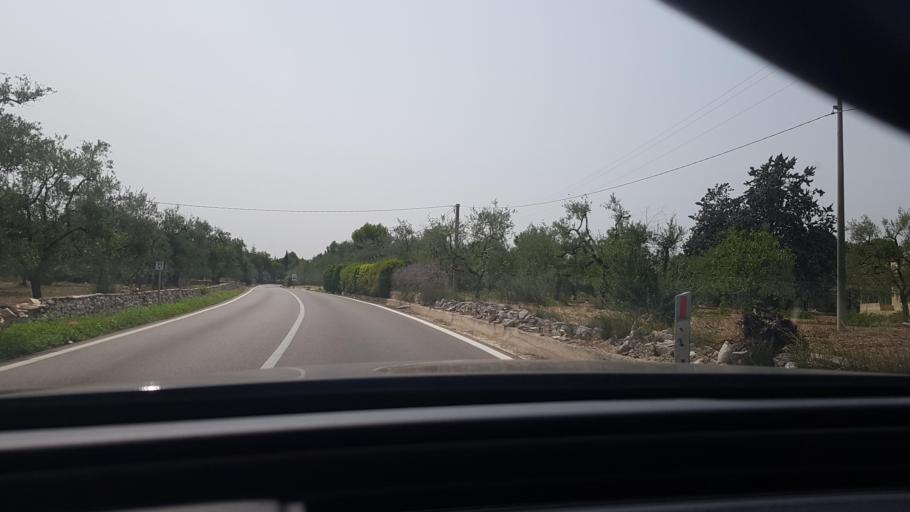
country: IT
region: Apulia
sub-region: Provincia di Barletta - Andria - Trani
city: Andria
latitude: 41.1492
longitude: 16.2908
